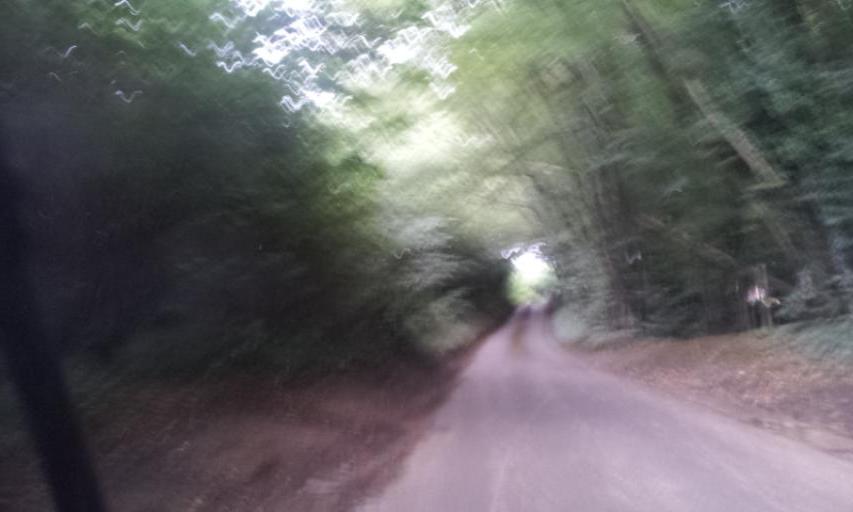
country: GB
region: England
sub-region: Kent
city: Wateringbury
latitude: 51.2678
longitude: 0.4558
